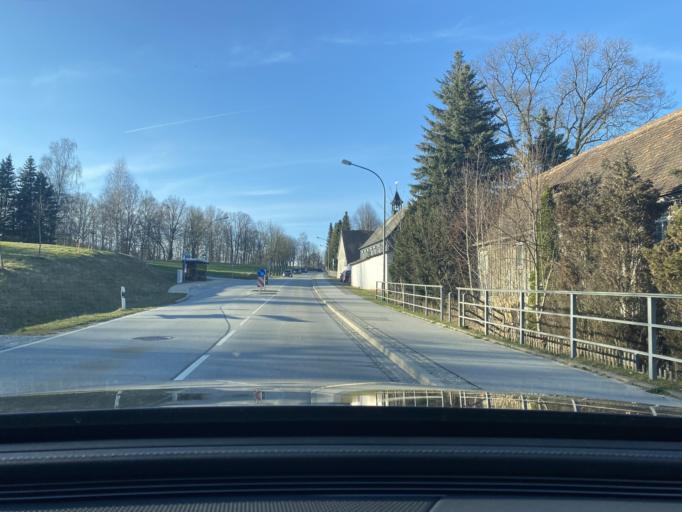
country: DE
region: Saxony
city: Schirgiswalde
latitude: 51.0616
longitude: 14.4306
